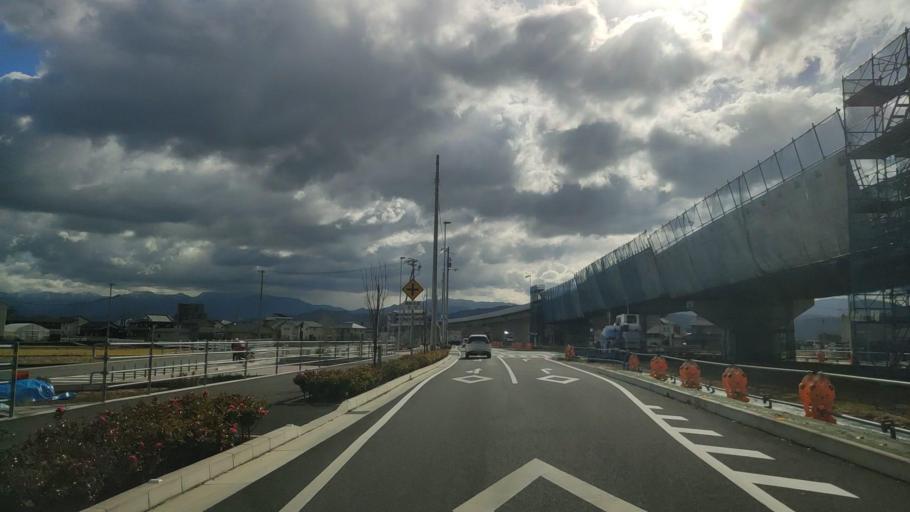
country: JP
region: Ehime
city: Masaki-cho
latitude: 33.8139
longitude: 132.7212
